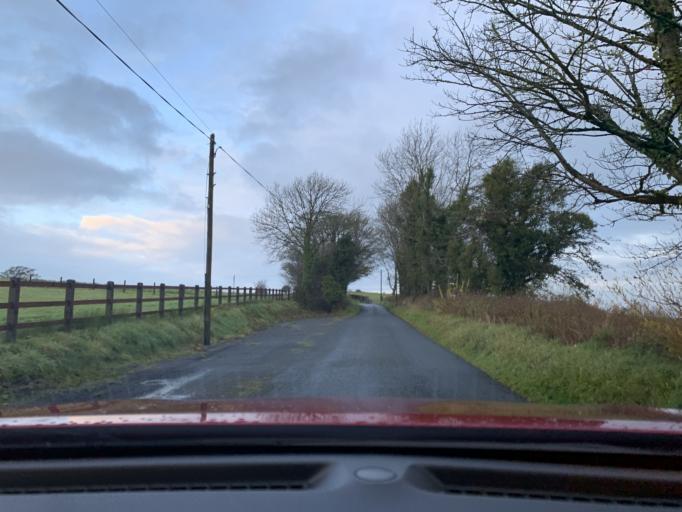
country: IE
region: Connaught
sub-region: Sligo
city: Ballymote
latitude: 54.0466
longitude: -8.5304
